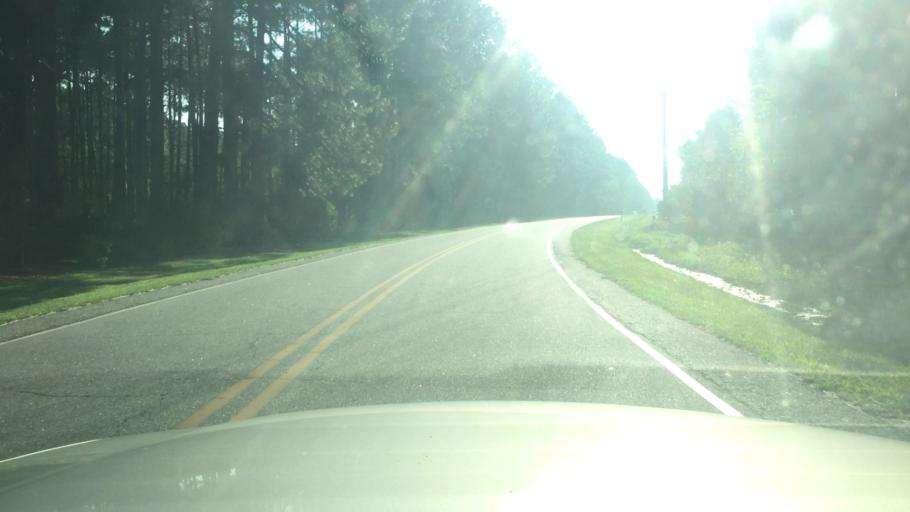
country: US
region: North Carolina
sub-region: Cumberland County
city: Spring Lake
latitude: 35.2061
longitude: -78.8867
